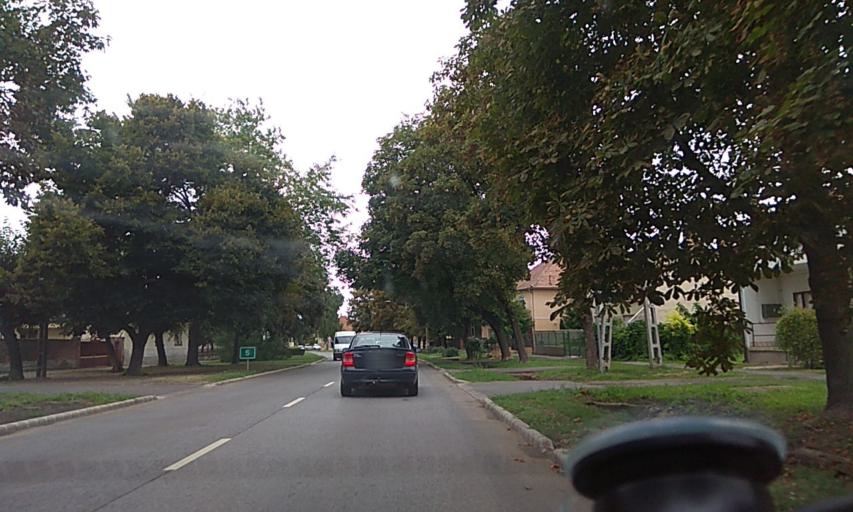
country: HU
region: Borsod-Abauj-Zemplen
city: Tarcal
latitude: 48.1303
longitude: 21.3443
